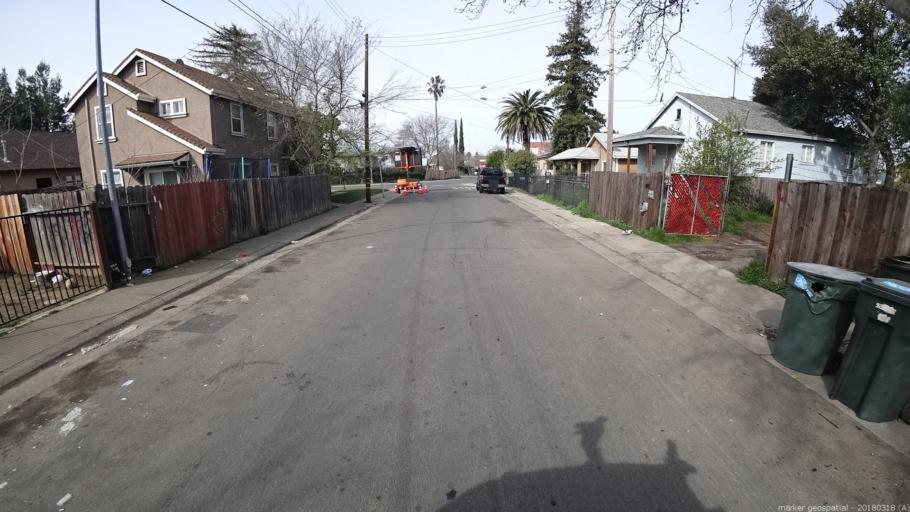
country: US
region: California
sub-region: Sacramento County
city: Parkway
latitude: 38.5383
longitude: -121.4582
